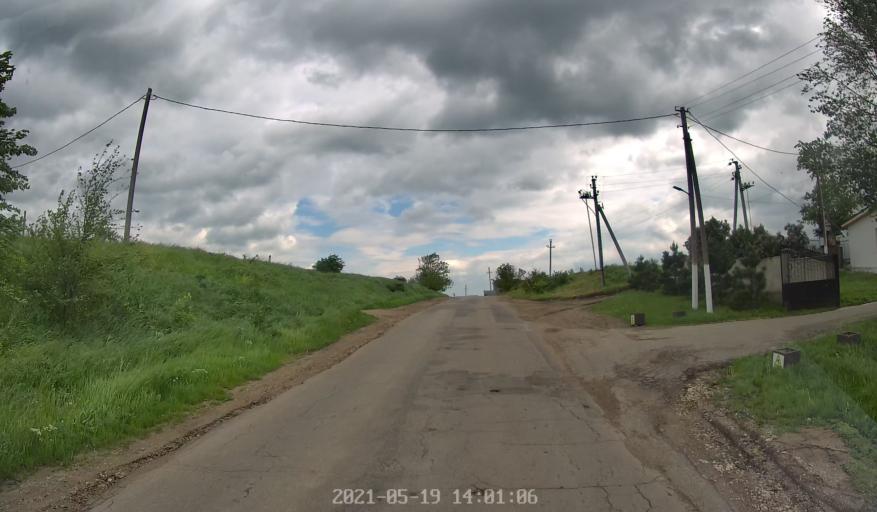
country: MD
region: Chisinau
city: Chisinau
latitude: 47.0327
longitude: 28.9351
